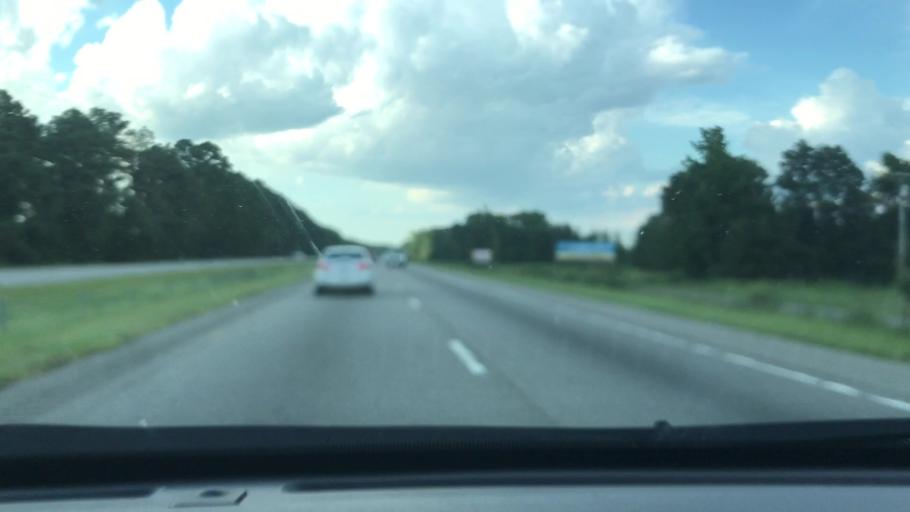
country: US
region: North Carolina
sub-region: Cumberland County
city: Hope Mills
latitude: 34.8941
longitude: -78.9593
